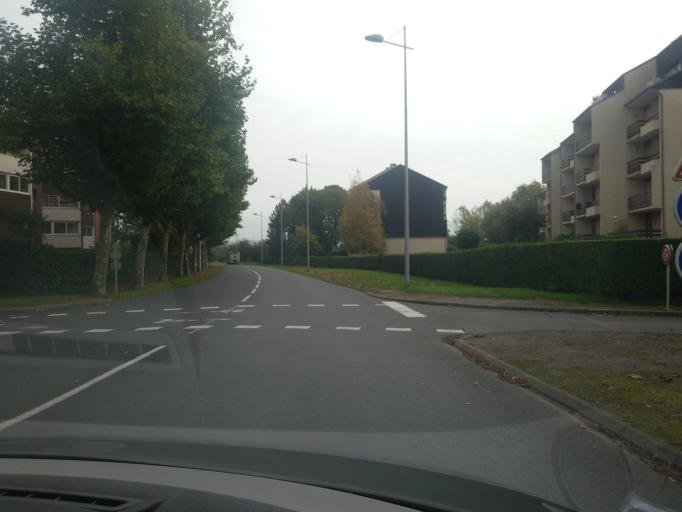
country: FR
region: Lower Normandy
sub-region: Departement du Calvados
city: Cabourg
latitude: 49.2834
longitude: -0.1242
